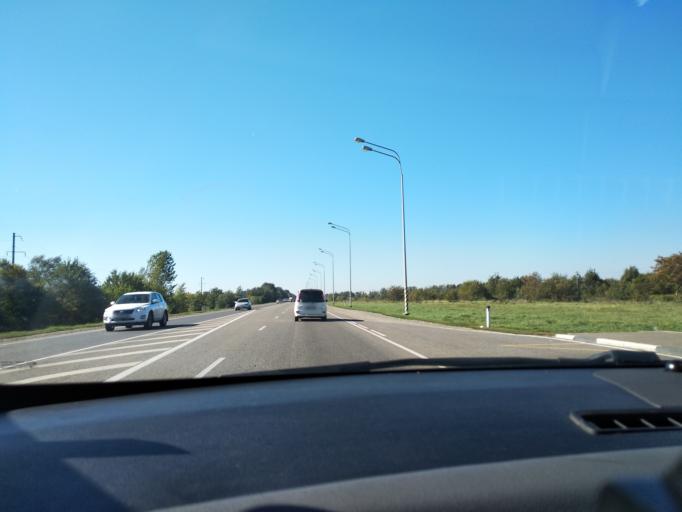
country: RU
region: Krasnodarskiy
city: Novotitarovskaya
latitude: 45.1554
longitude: 39.0691
